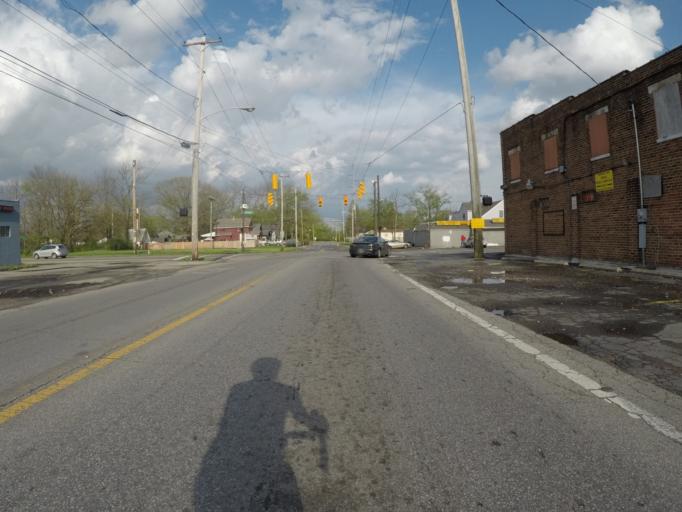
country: US
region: Ohio
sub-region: Franklin County
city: Bexley
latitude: 40.0132
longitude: -82.9568
